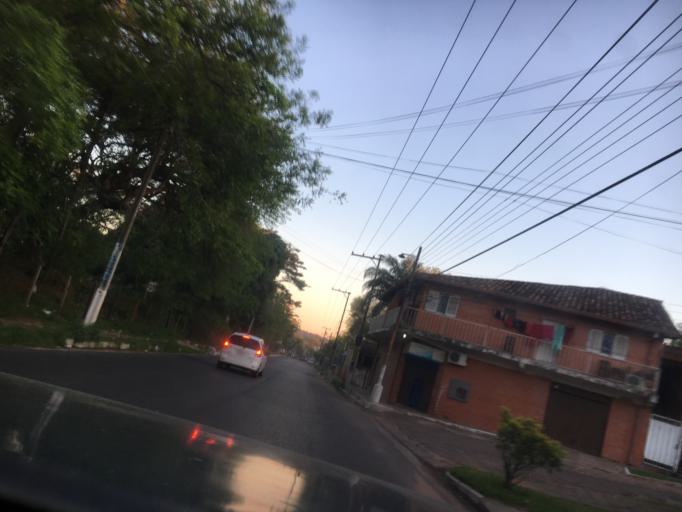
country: PY
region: Central
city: Lambare
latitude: -25.3447
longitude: -57.6022
